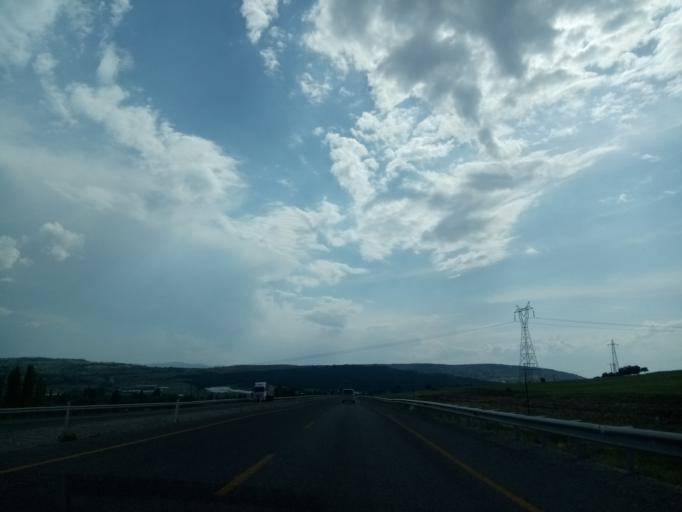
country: TR
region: Isparta
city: Bagkonak
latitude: 38.1981
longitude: 31.2511
